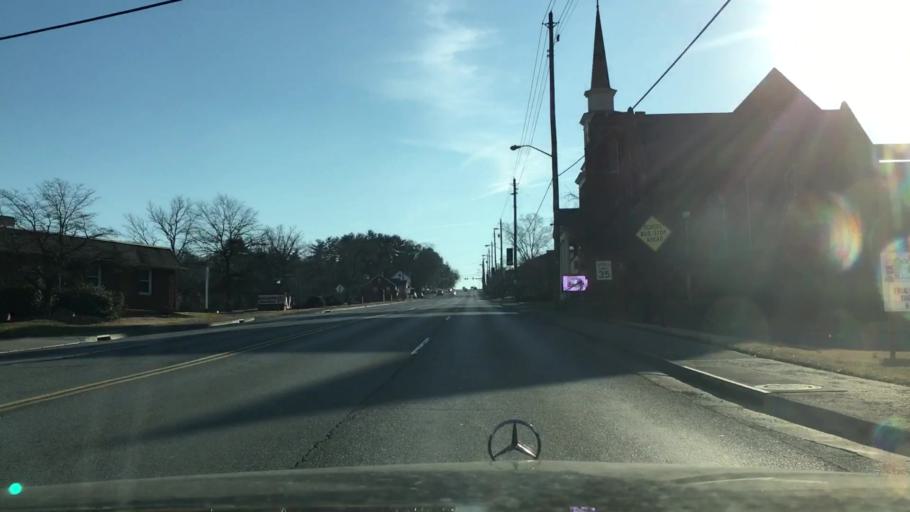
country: US
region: Virginia
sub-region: Roanoke County
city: Vinton
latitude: 37.2798
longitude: -79.8924
